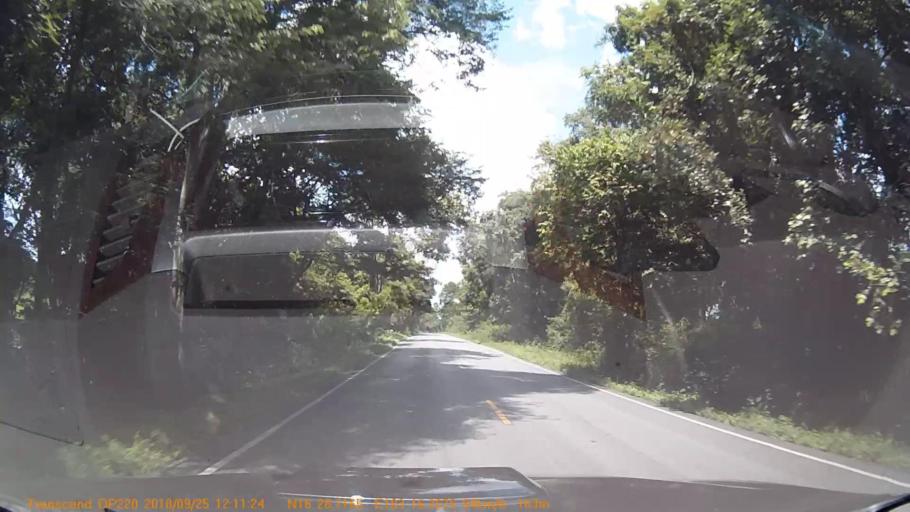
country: TH
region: Kalasin
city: Huai Mek
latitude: 16.4788
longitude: 103.2710
